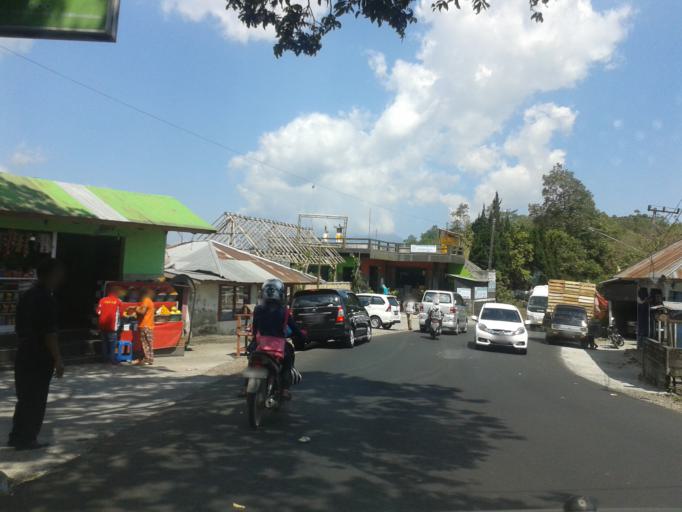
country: ID
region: Bali
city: Banjar Kedisan
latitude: -8.2812
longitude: 115.3619
